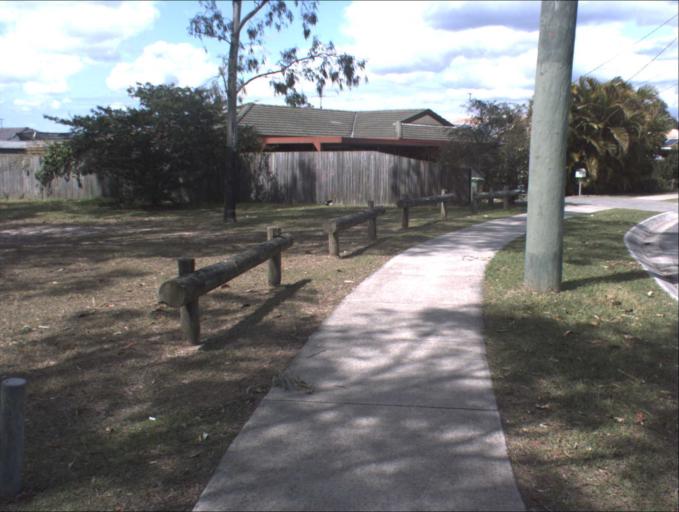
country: AU
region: Queensland
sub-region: Logan
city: Logan City
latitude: -27.6719
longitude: 153.0877
